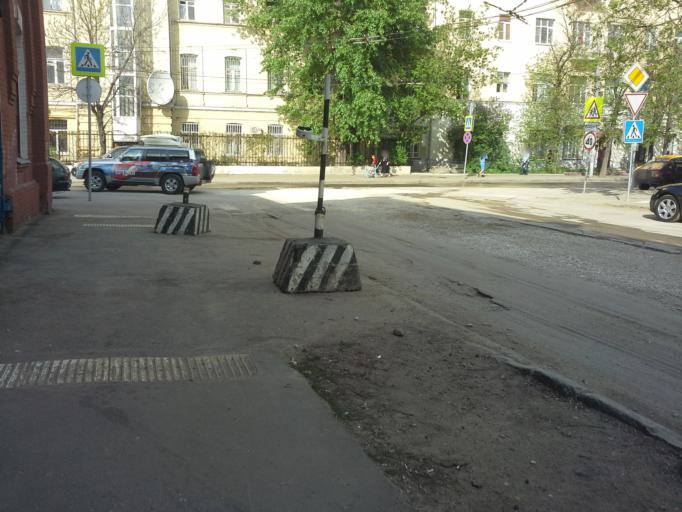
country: RU
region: Moscow
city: Mar'ina Roshcha
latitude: 55.7801
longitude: 37.5941
